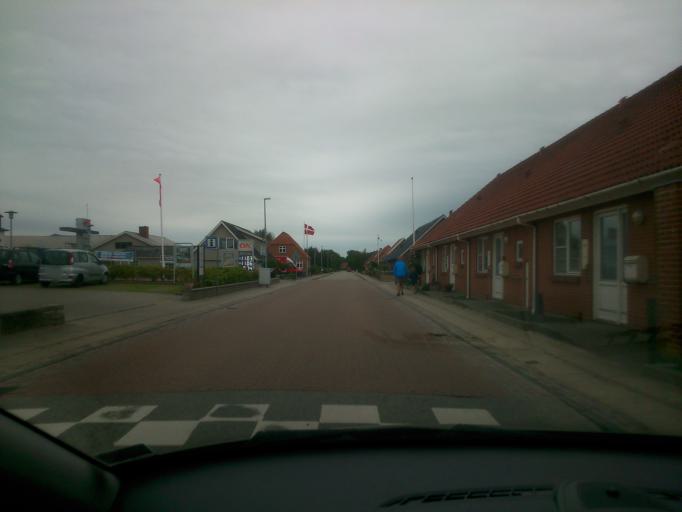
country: DK
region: Central Jutland
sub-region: Ringkobing-Skjern Kommune
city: Skjern
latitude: 55.9637
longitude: 8.3721
